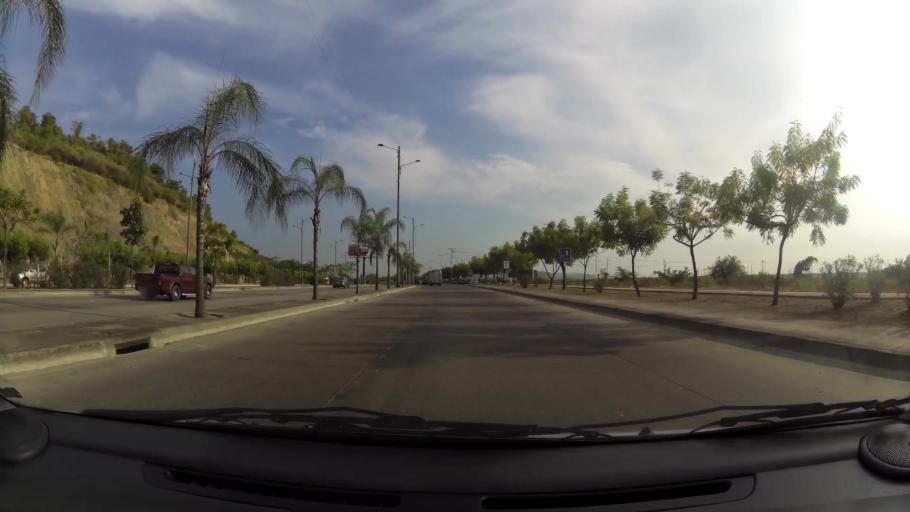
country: EC
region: Guayas
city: Eloy Alfaro
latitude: -2.0717
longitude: -79.8976
